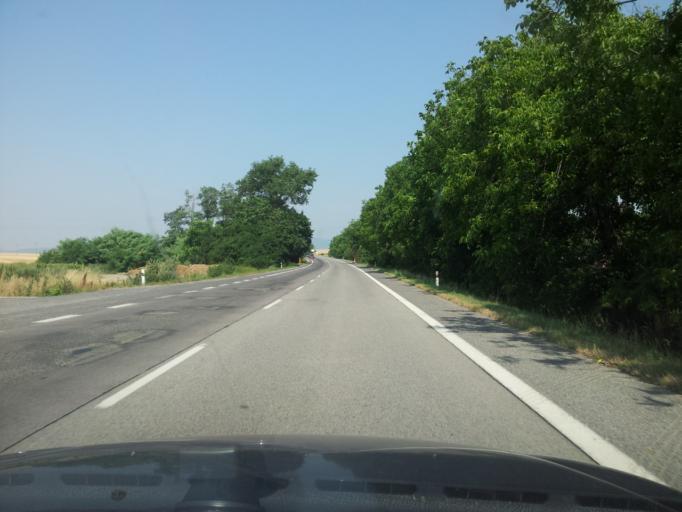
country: SK
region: Nitriansky
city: Zlate Moravce
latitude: 48.3691
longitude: 18.4410
